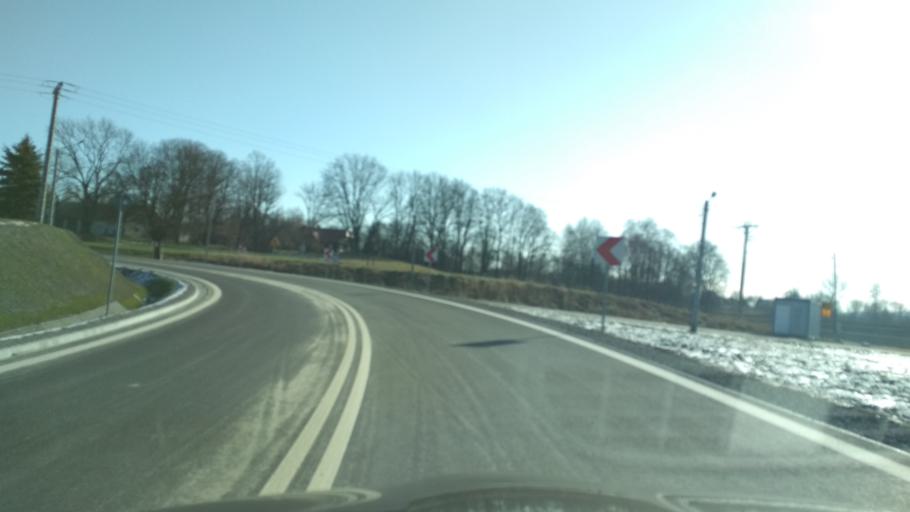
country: PL
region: Subcarpathian Voivodeship
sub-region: Powiat ropczycko-sedziszowski
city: Sedziszow Malopolski
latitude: 50.0703
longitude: 21.7332
